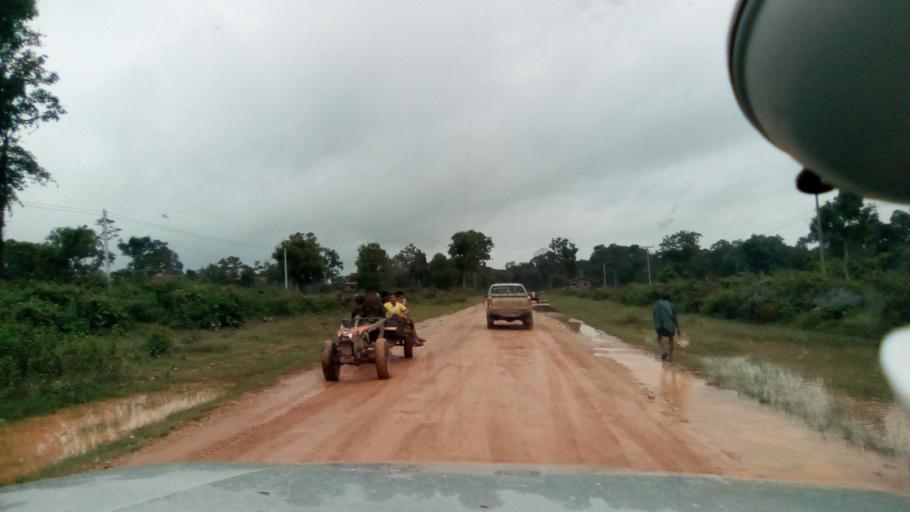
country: LA
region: Attapu
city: Attapu
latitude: 14.6755
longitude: 106.5670
